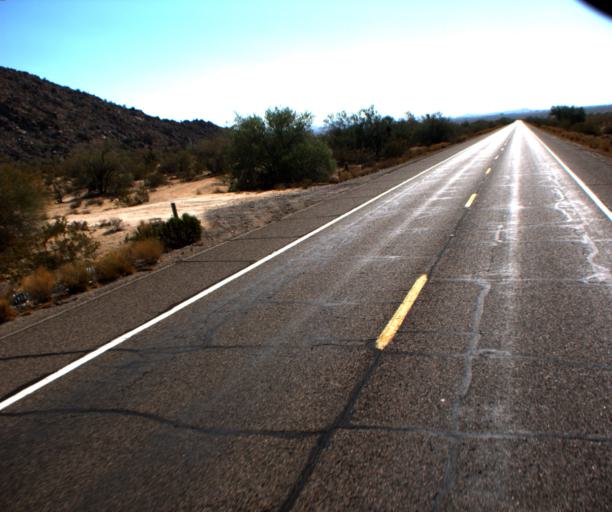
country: US
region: Arizona
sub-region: Pinal County
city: Blackwater
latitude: 33.0180
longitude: -111.6547
